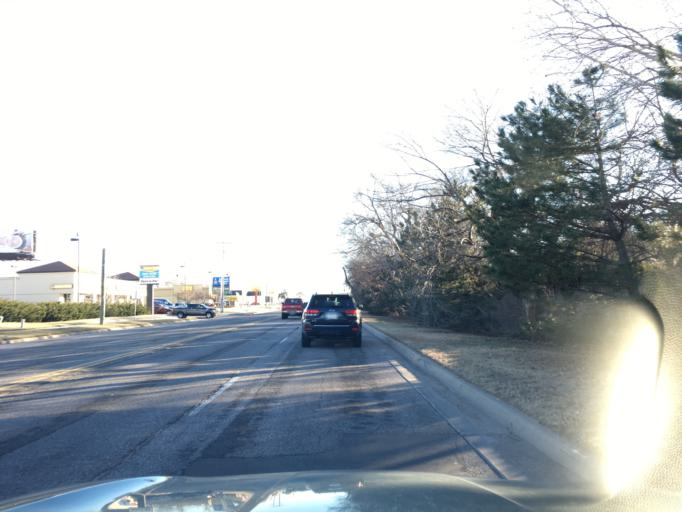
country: US
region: Kansas
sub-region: Sedgwick County
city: Bellaire
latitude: 37.6997
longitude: -97.2263
